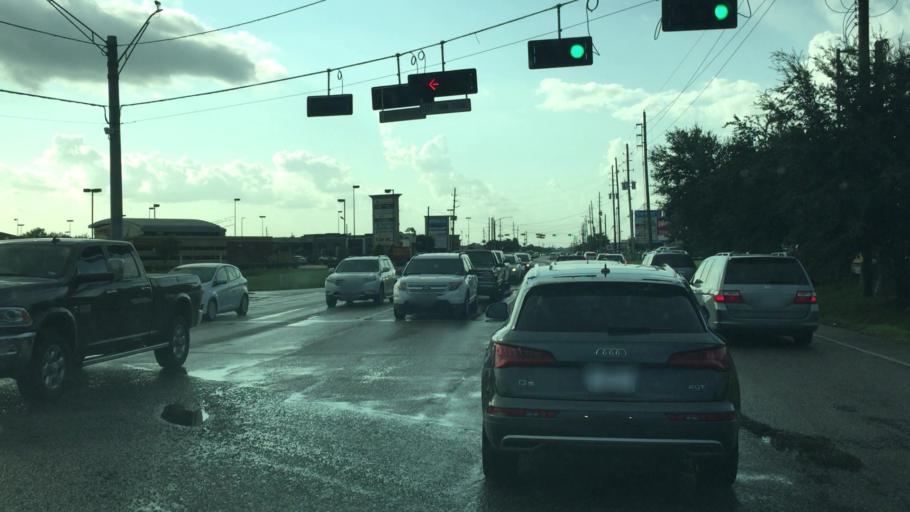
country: US
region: Texas
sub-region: Montgomery County
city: The Woodlands
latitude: 30.0741
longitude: -95.5134
